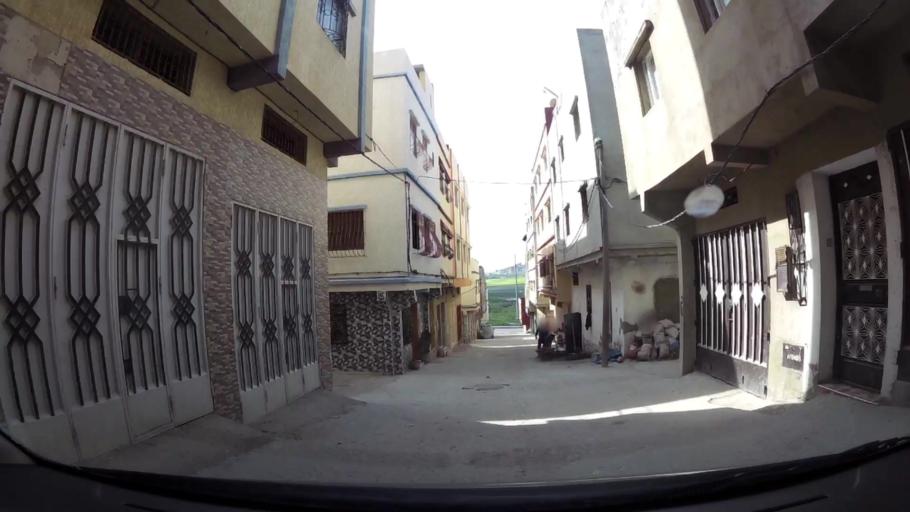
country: MA
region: Tanger-Tetouan
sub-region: Tanger-Assilah
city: Tangier
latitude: 35.7651
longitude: -5.7728
